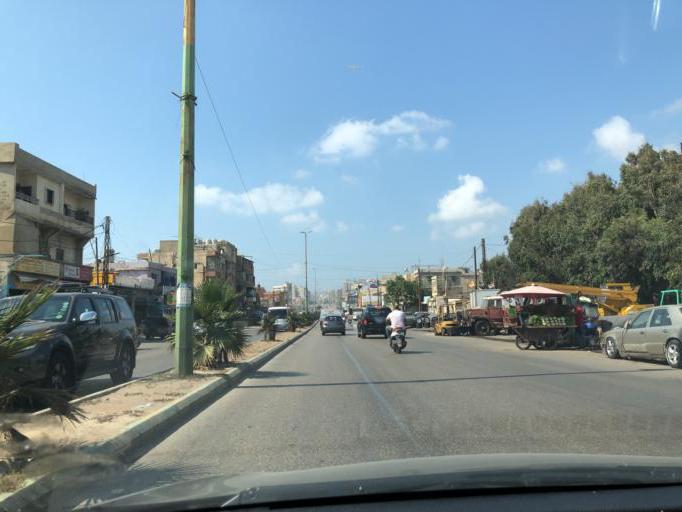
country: LB
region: Beyrouth
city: Beirut
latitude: 33.8527
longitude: 35.4853
